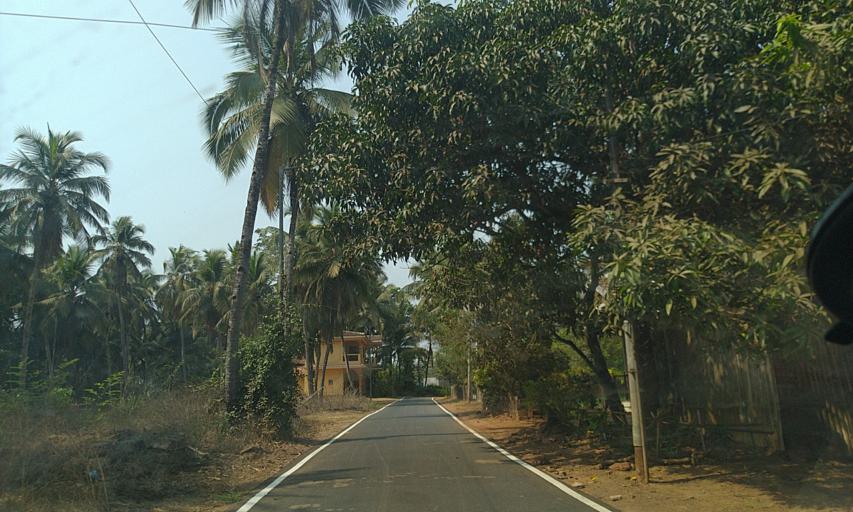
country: IN
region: Goa
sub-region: South Goa
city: Raia
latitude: 15.3031
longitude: 73.9459
